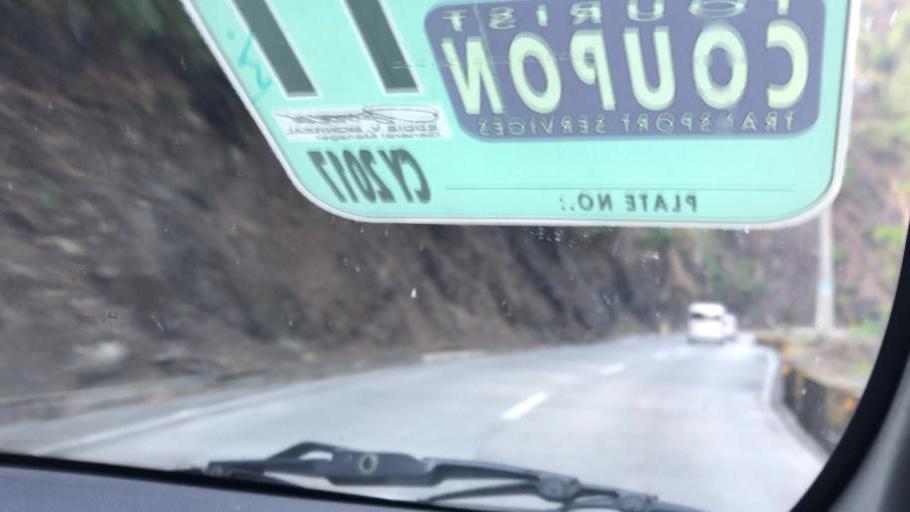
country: PH
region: Cordillera
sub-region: Province of Benguet
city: Tuba
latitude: 16.3256
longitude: 120.6137
